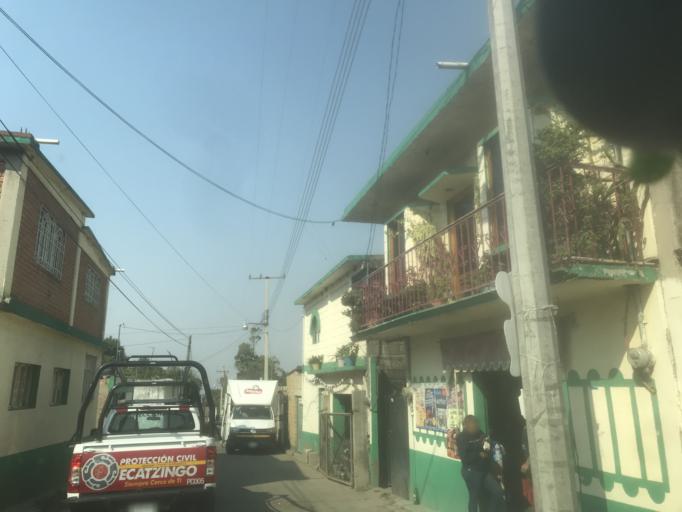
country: MX
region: Morelos
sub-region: Yecapixtla
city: Texcala
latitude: 18.9339
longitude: -98.7965
